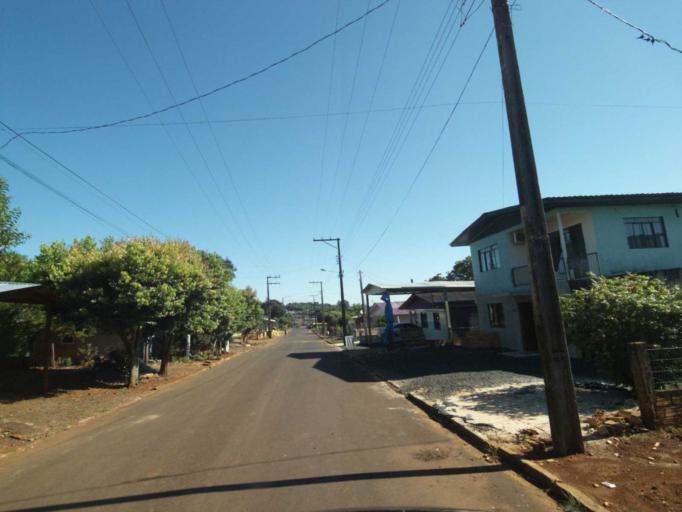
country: BR
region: Parana
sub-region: Coronel Vivida
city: Coronel Vivida
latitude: -25.9602
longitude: -52.8119
